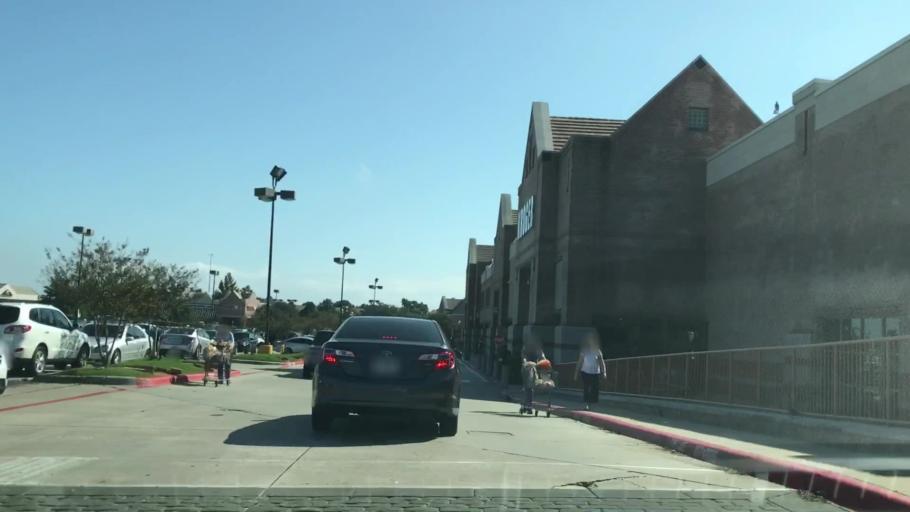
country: US
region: Texas
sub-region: Dallas County
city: Farmers Branch
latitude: 32.9094
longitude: -96.9608
